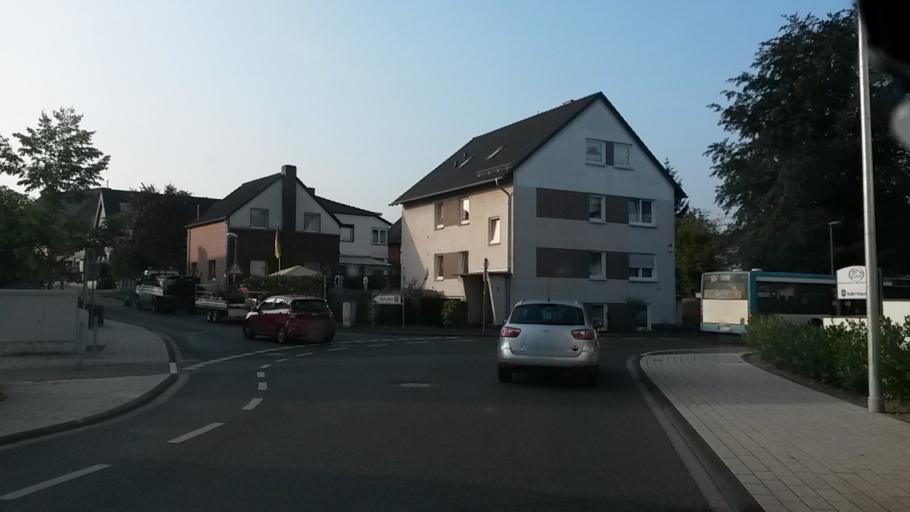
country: DE
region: North Rhine-Westphalia
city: Lohmar
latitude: 50.8399
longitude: 7.2133
